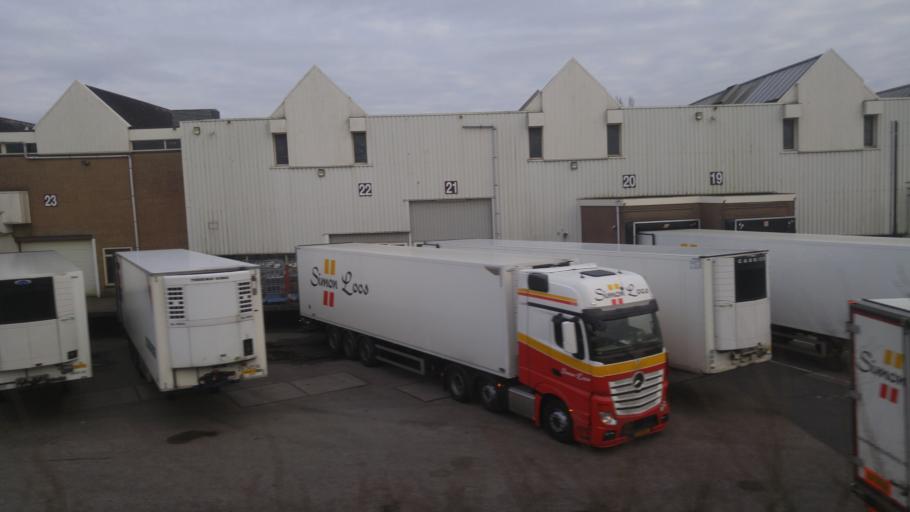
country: NL
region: Utrecht
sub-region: Gemeente Woerden
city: Woerden
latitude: 52.0805
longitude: 4.8849
